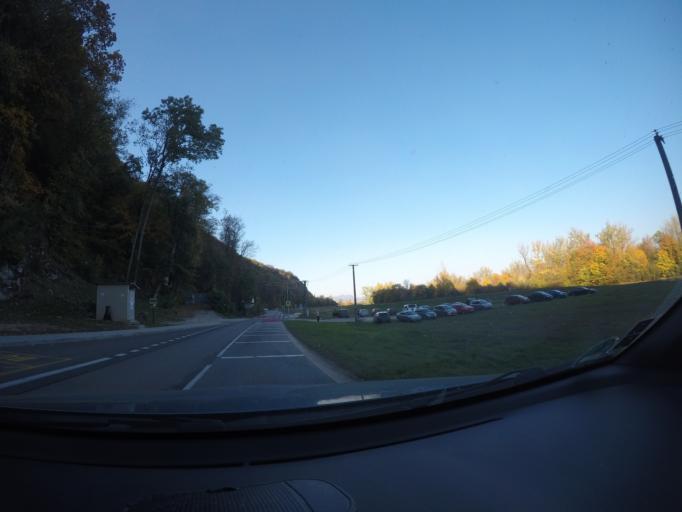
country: SK
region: Trenciansky
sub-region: Okres Trencin
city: Trencin
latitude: 48.9154
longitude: 18.0737
